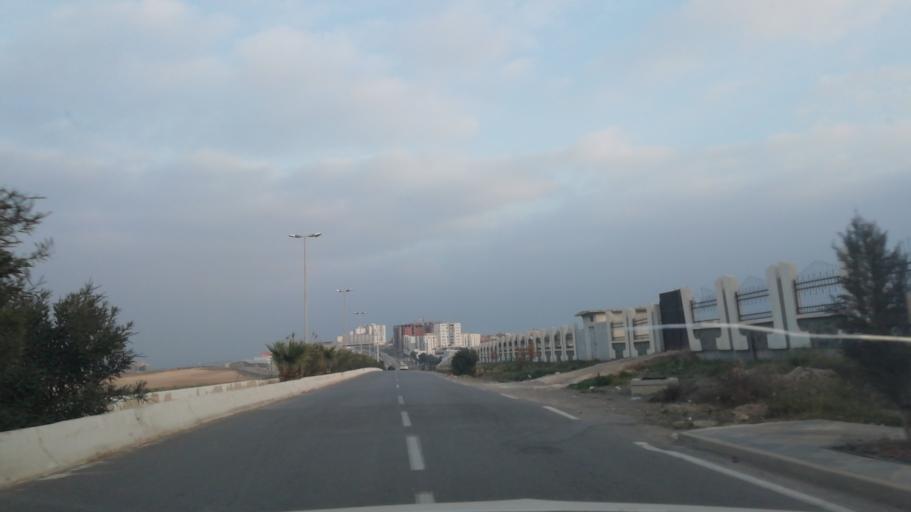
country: DZ
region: Sidi Bel Abbes
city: Sidi Bel Abbes
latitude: 35.2254
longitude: -0.6356
